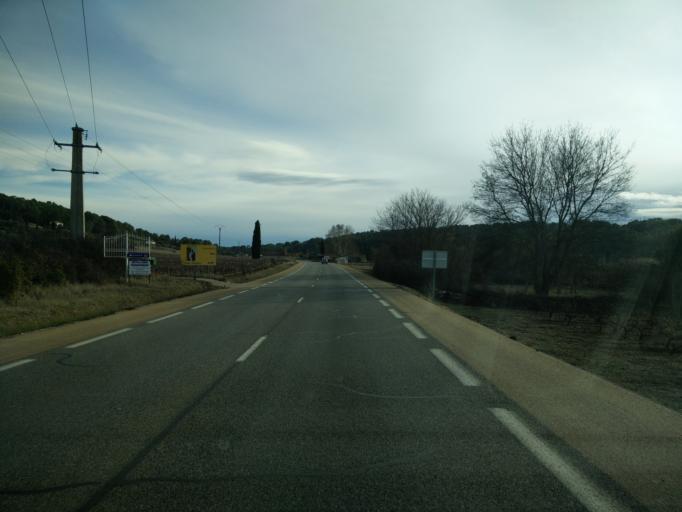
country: FR
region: Provence-Alpes-Cote d'Azur
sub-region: Departement du Var
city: Lorgues
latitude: 43.4789
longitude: 6.3723
